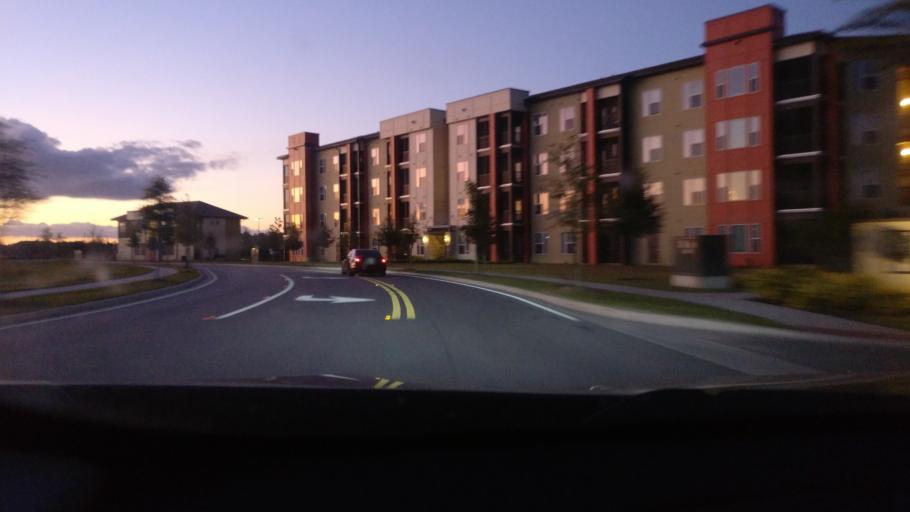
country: US
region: Florida
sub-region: Orange County
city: Hunters Creek
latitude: 28.3453
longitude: -81.4710
